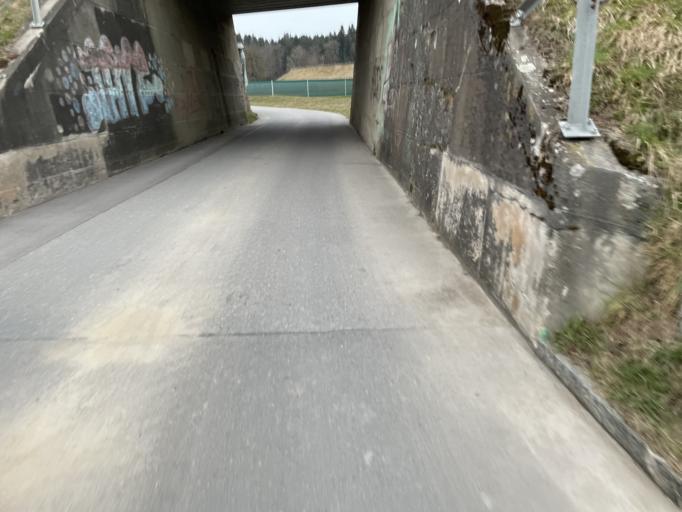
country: CH
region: Bern
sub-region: Bern-Mittelland District
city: Rubigen
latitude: 46.9063
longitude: 7.5412
